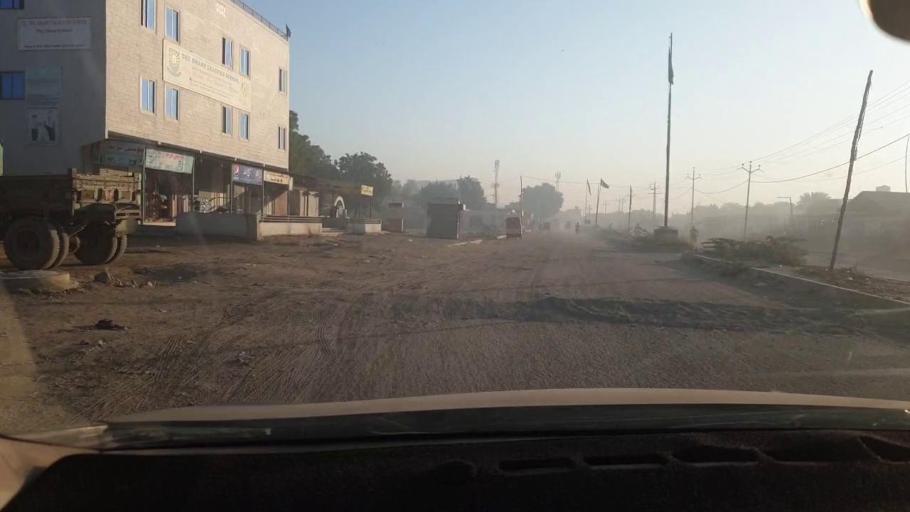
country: PK
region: Sindh
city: Malir Cantonment
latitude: 25.0107
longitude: 67.1642
